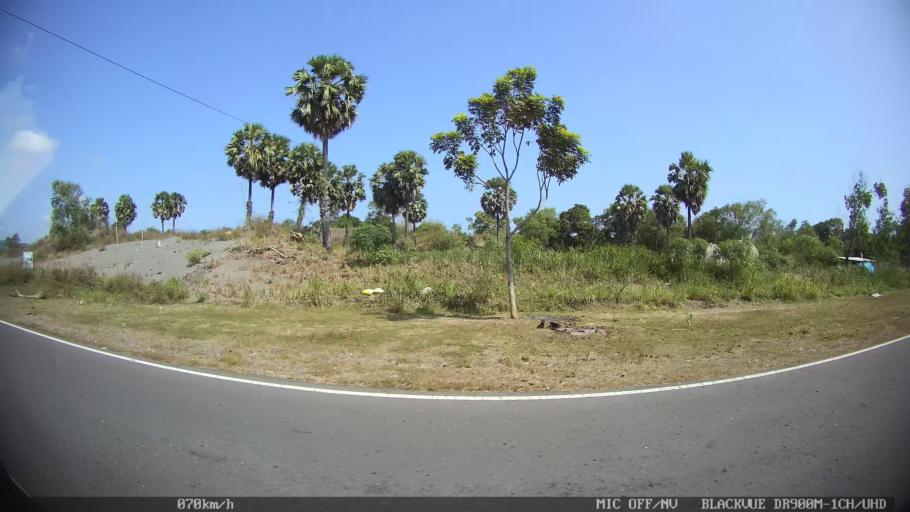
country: ID
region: Daerah Istimewa Yogyakarta
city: Bambanglipuro
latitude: -8.0109
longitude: 110.3076
